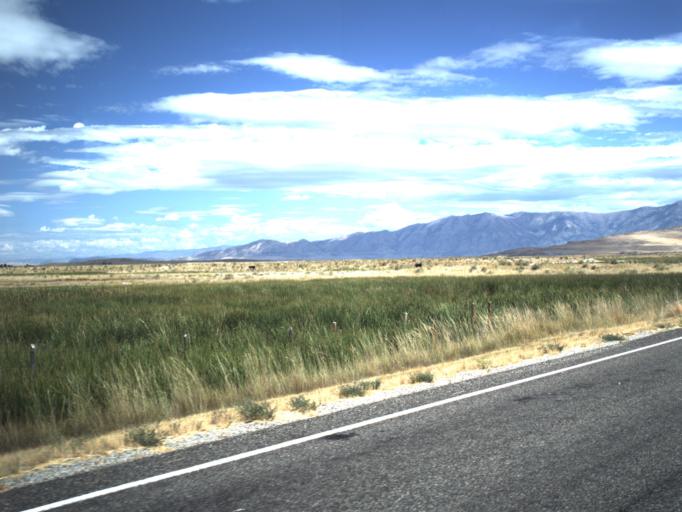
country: US
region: Utah
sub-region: Box Elder County
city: Tremonton
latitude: 41.6099
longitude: -112.3410
